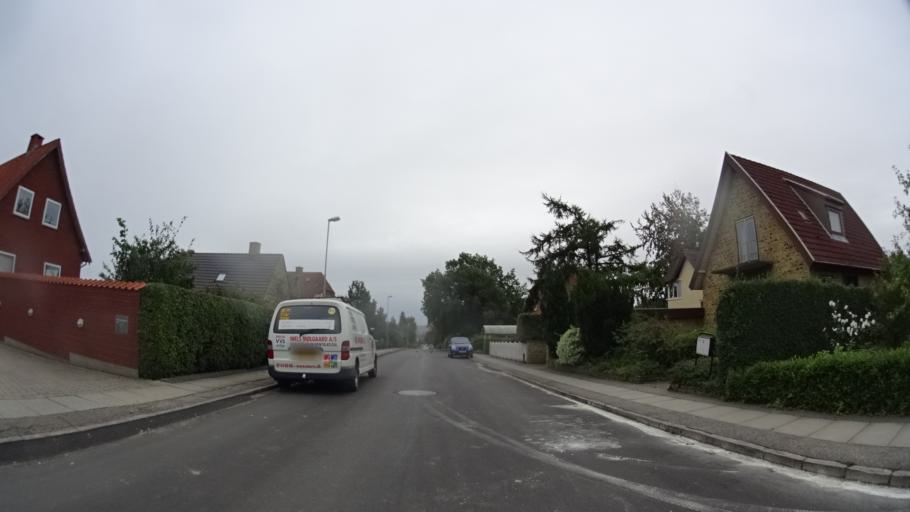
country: DK
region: Central Jutland
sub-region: Arhus Kommune
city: Stavtrup
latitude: 56.1573
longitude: 10.1457
